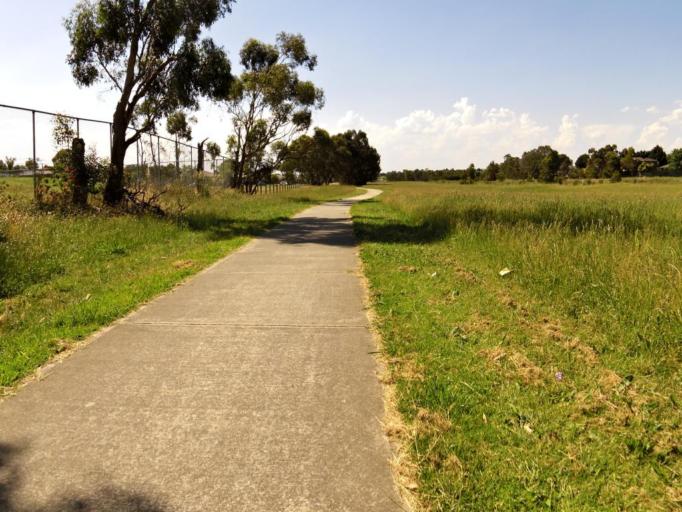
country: AU
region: Victoria
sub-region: Casey
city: Narre Warren South
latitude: -38.0426
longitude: 145.2755
